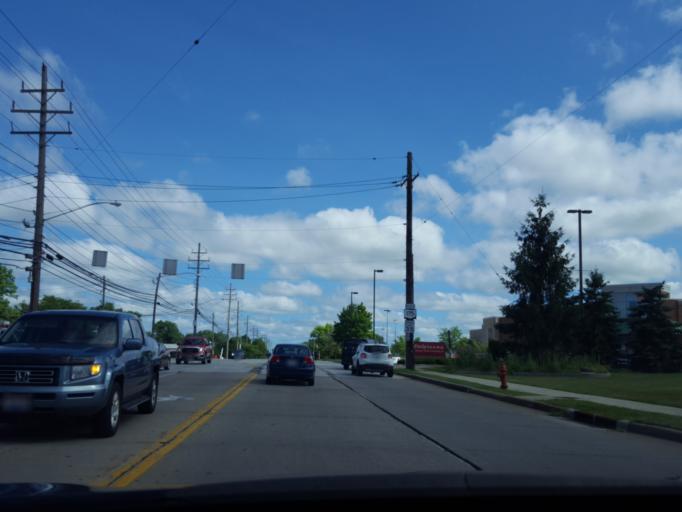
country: US
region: Ohio
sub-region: Cuyahoga County
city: Richmond Heights
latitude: 41.5392
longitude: -81.4971
